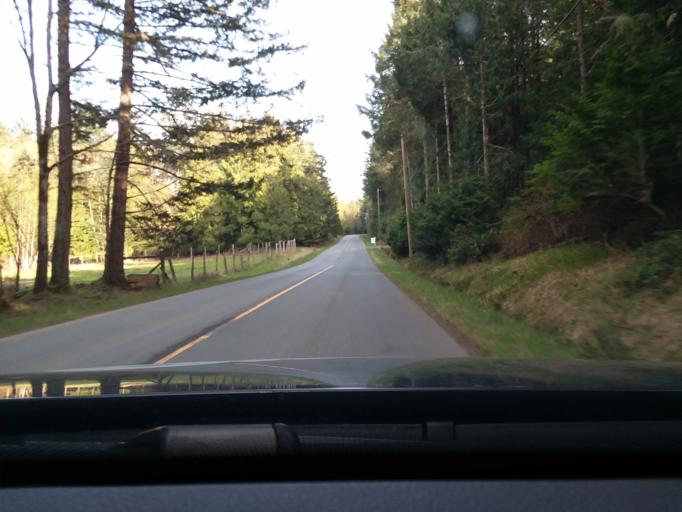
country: CA
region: British Columbia
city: North Saanich
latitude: 48.7500
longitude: -123.2609
